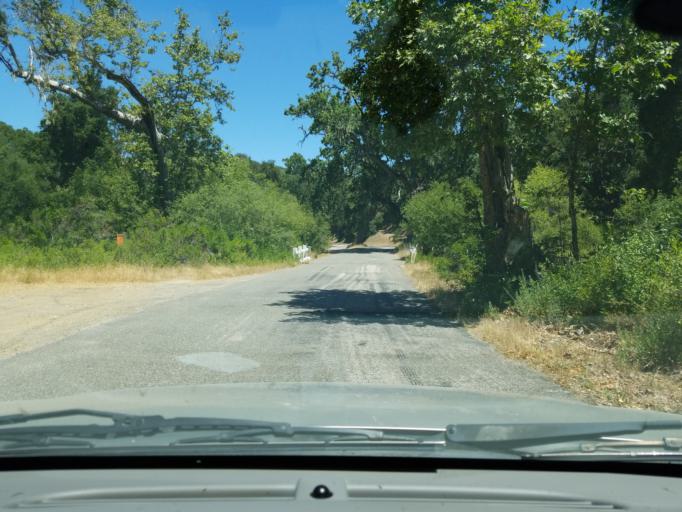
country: US
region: California
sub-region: Monterey County
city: Gonzales
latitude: 36.3474
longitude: -121.5429
